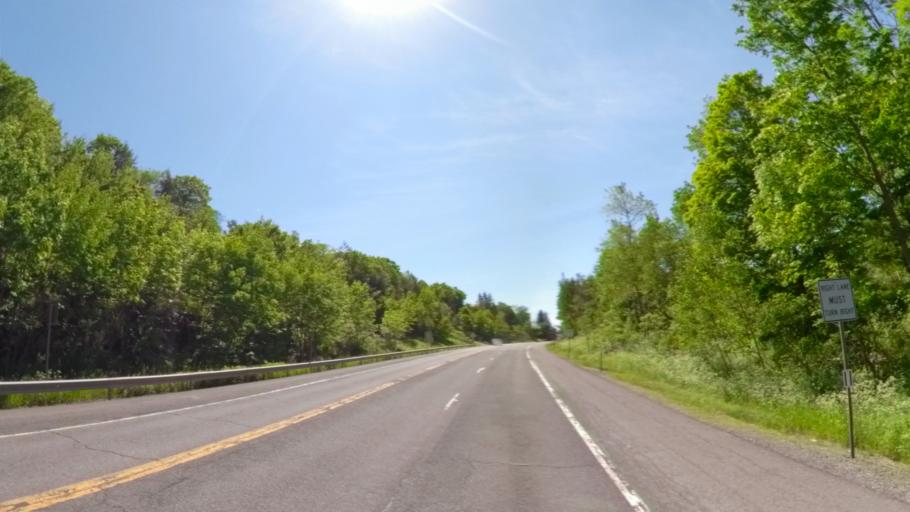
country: US
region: New York
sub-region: Delaware County
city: Stamford
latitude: 42.1487
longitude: -74.4965
